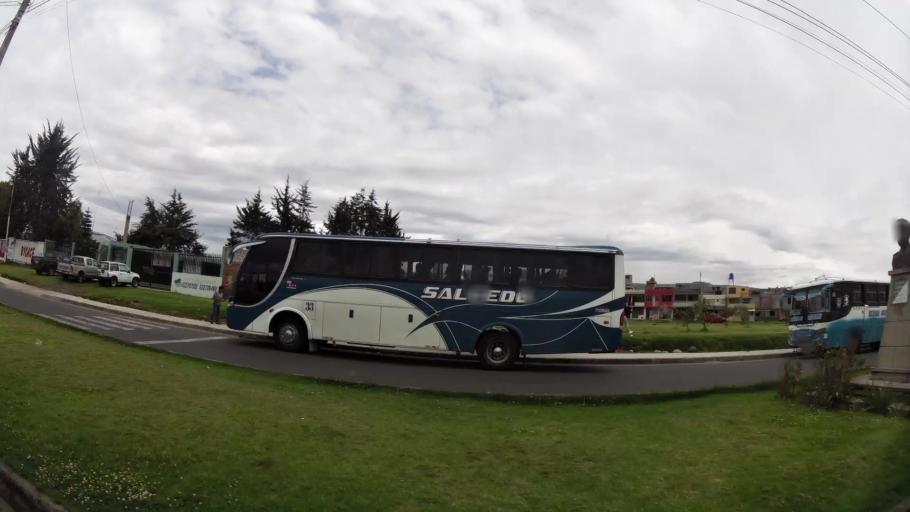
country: EC
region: Cotopaxi
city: San Miguel de Salcedo
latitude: -1.0314
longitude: -78.5906
